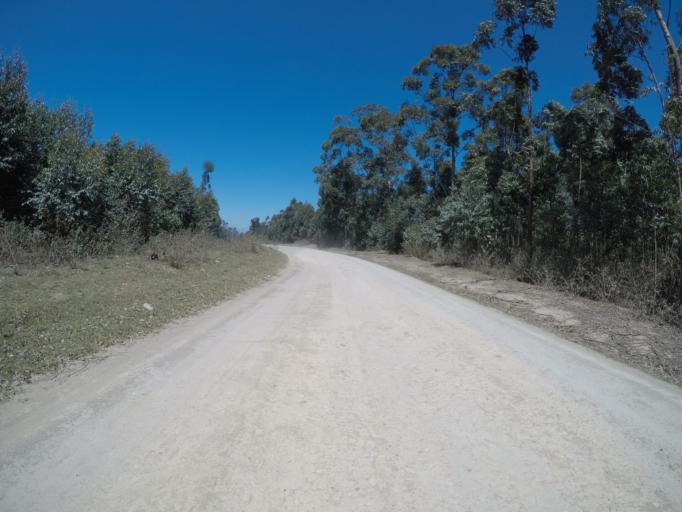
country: ZA
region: Eastern Cape
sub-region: OR Tambo District Municipality
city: Libode
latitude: -31.9575
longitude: 29.0234
